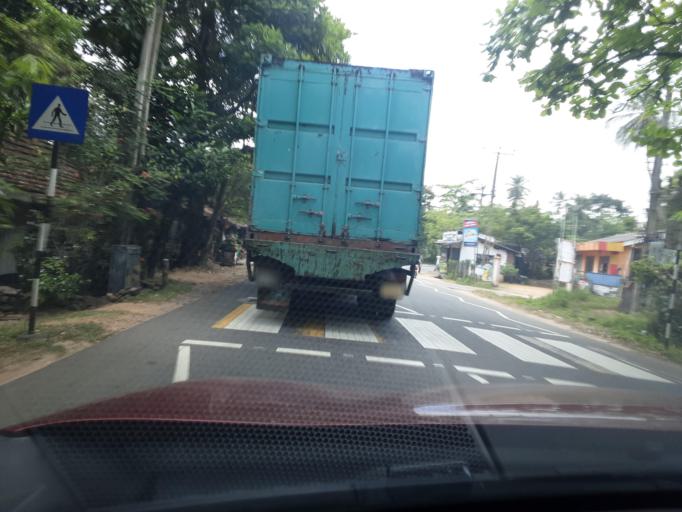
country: LK
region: North Western
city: Kurunegala
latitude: 7.4461
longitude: 80.2034
